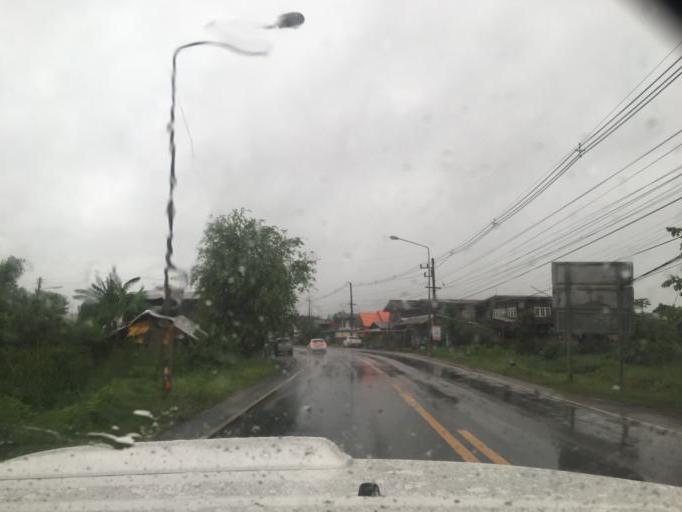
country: TH
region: Changwat Udon Thani
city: Udon Thani
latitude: 17.3670
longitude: 102.7209
